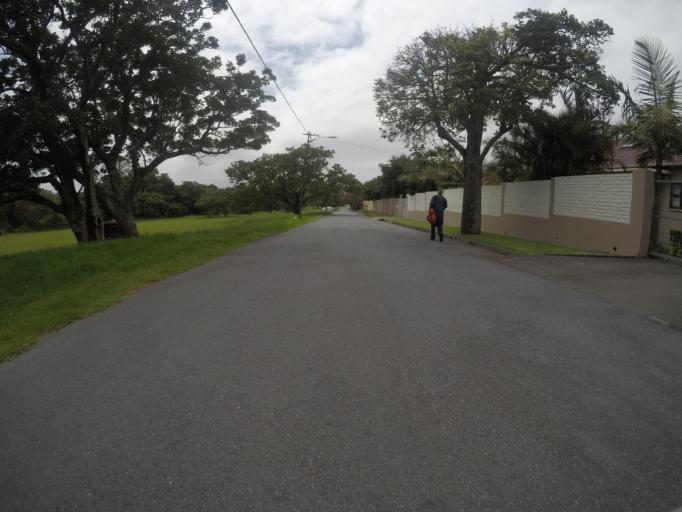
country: ZA
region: Eastern Cape
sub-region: Buffalo City Metropolitan Municipality
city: East London
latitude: -32.9897
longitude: 27.9215
